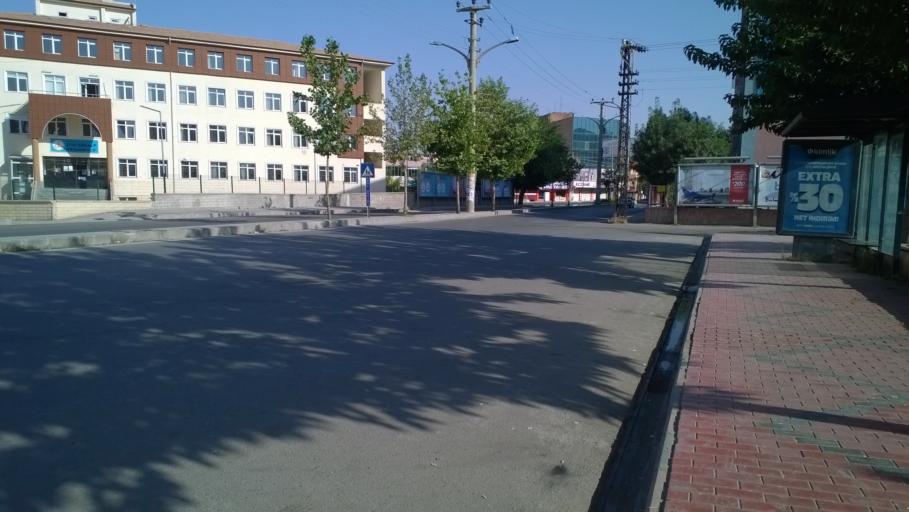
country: TR
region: Batman
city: Batman
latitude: 37.8895
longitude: 41.1252
